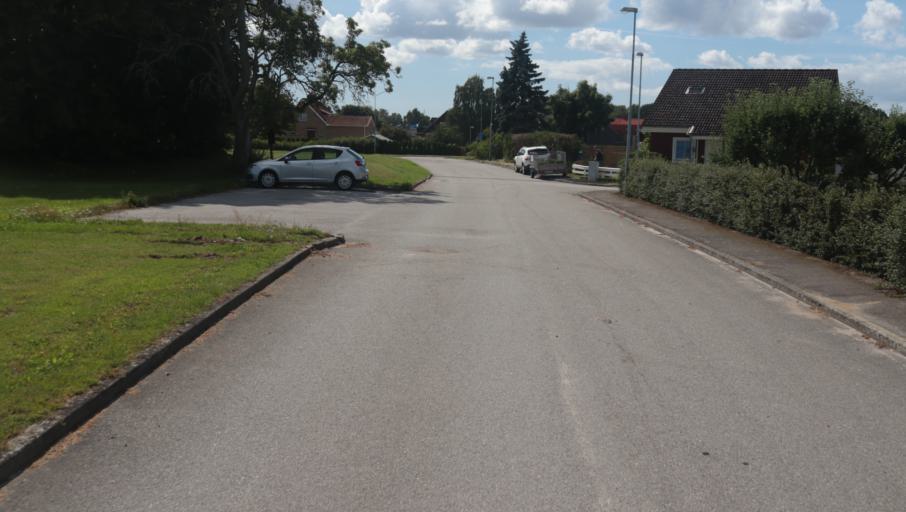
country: SE
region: Blekinge
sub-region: Karlshamns Kommun
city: Morrum
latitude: 56.1965
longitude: 14.7433
